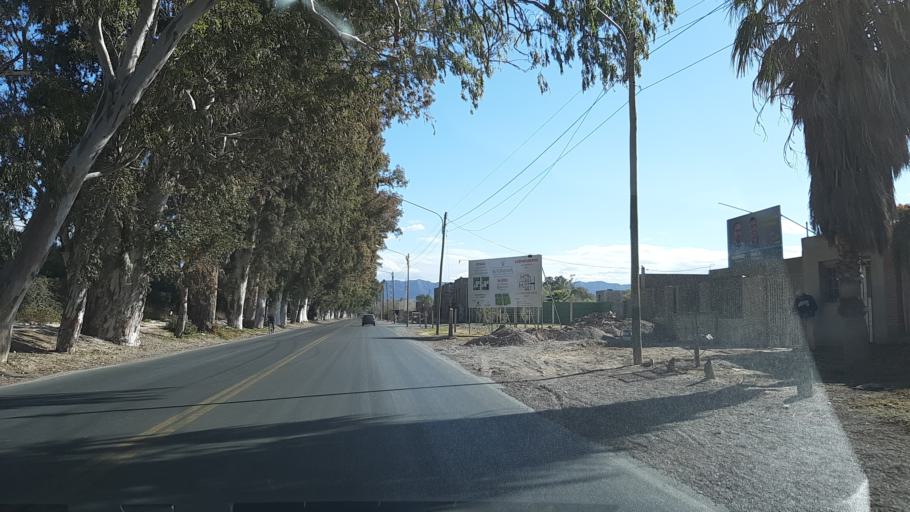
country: AR
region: San Juan
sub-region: Departamento de Rivadavia
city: Rivadavia
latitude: -31.5388
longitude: -68.5968
